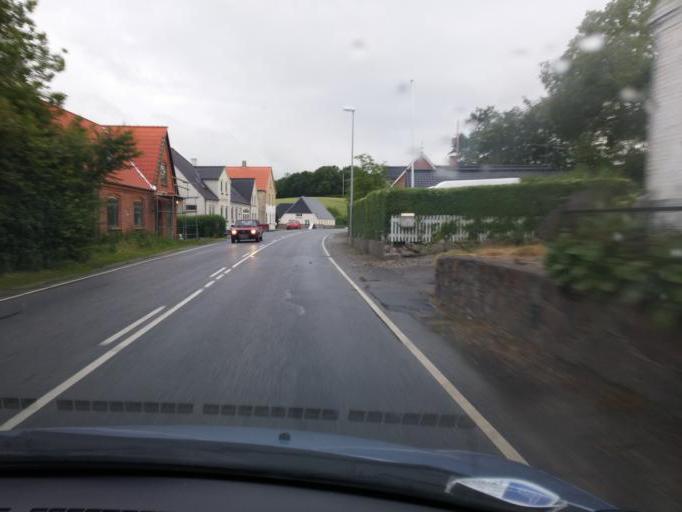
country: DK
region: South Denmark
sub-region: Kerteminde Kommune
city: Kerteminde
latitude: 55.5158
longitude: 10.6552
